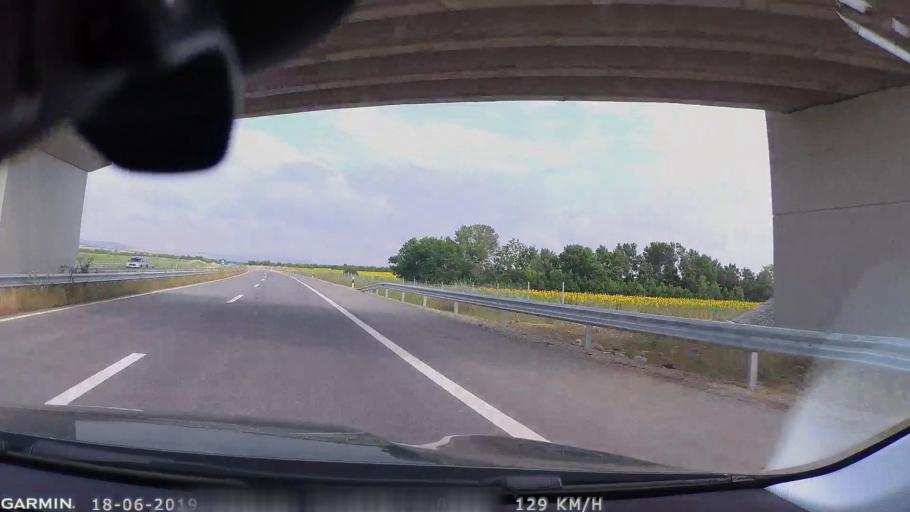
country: MK
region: Sveti Nikole
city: Sveti Nikole
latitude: 41.8272
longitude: 22.0055
